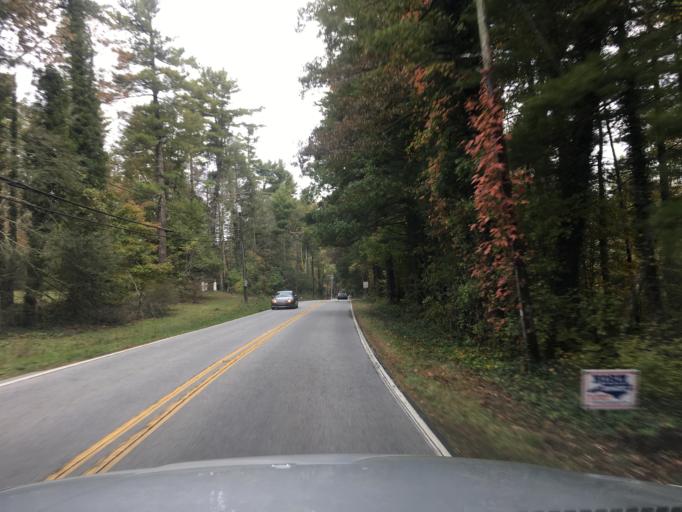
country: US
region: North Carolina
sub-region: Henderson County
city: Flat Rock
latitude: 35.2578
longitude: -82.4378
